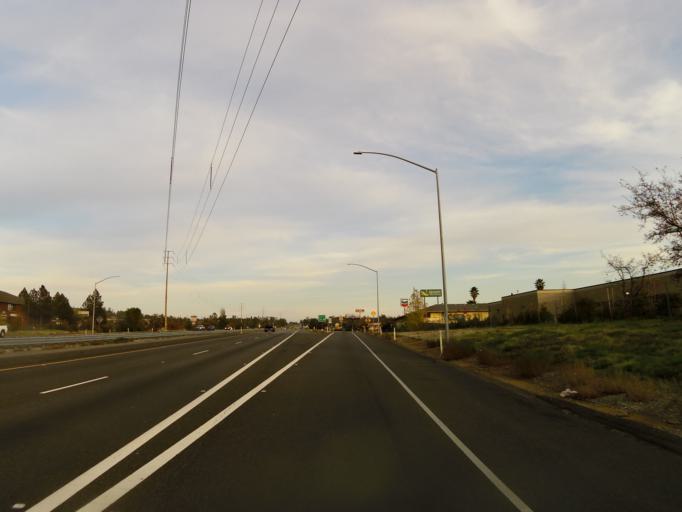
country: US
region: California
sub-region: El Dorado County
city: Cameron Park
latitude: 38.6593
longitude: -120.9723
